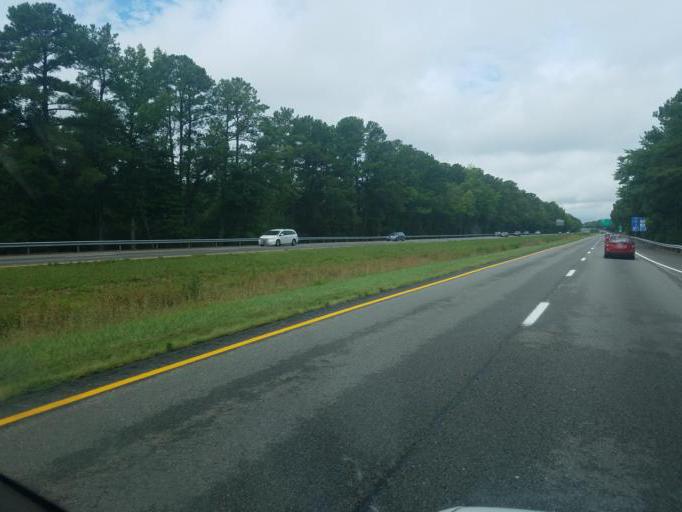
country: US
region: Virginia
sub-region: Henrico County
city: Sandston
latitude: 37.5272
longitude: -77.2973
